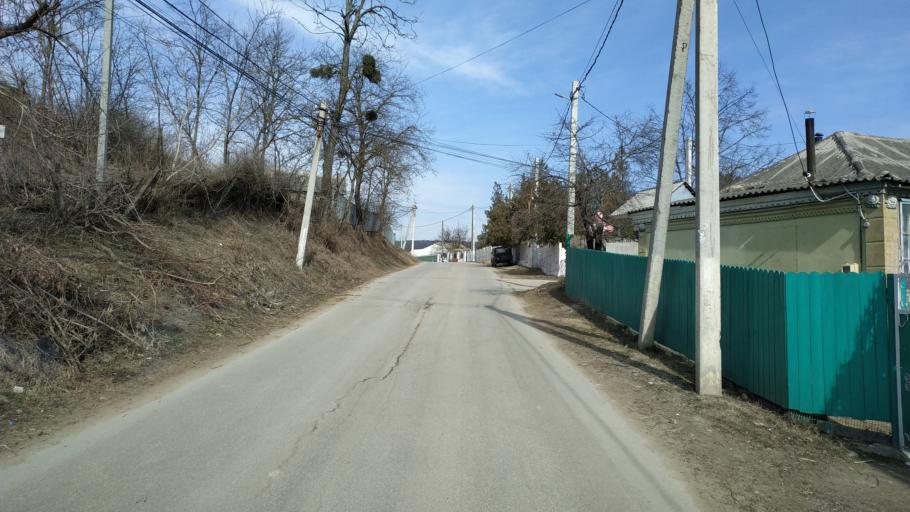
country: MD
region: Nisporeni
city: Nisporeni
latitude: 47.1999
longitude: 28.0647
